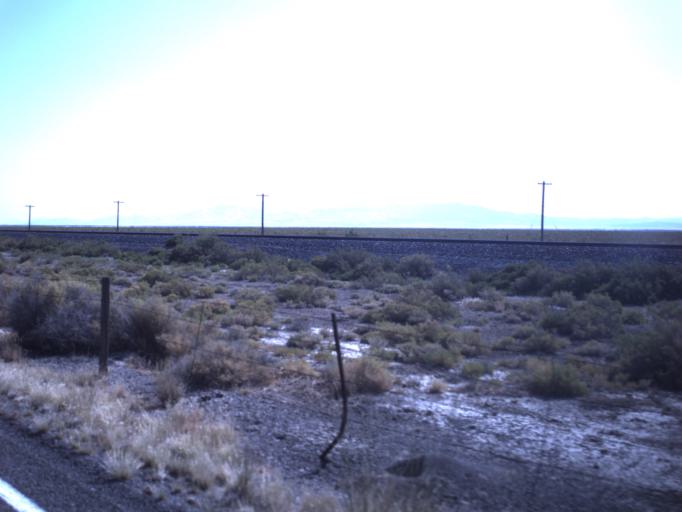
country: US
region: Utah
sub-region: Millard County
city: Delta
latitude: 39.1545
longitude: -112.7165
